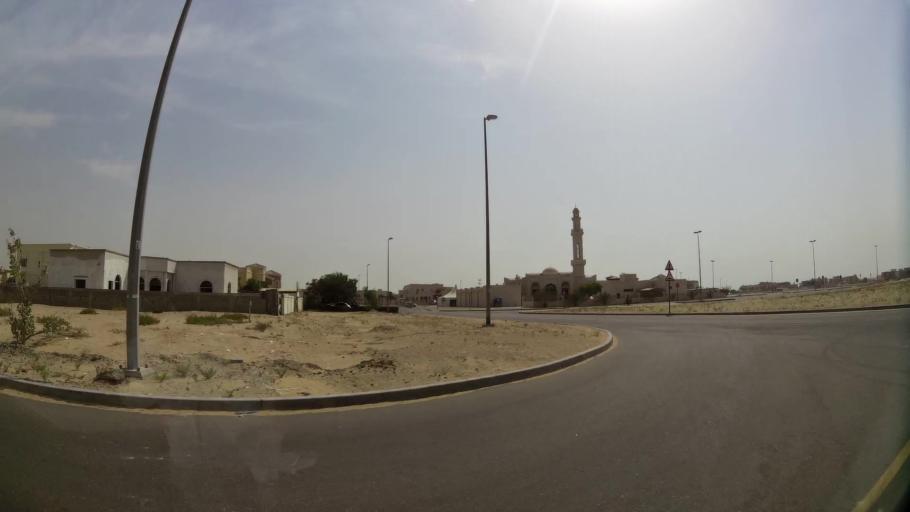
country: AE
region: Ash Shariqah
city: Sharjah
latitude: 25.2621
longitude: 55.4657
